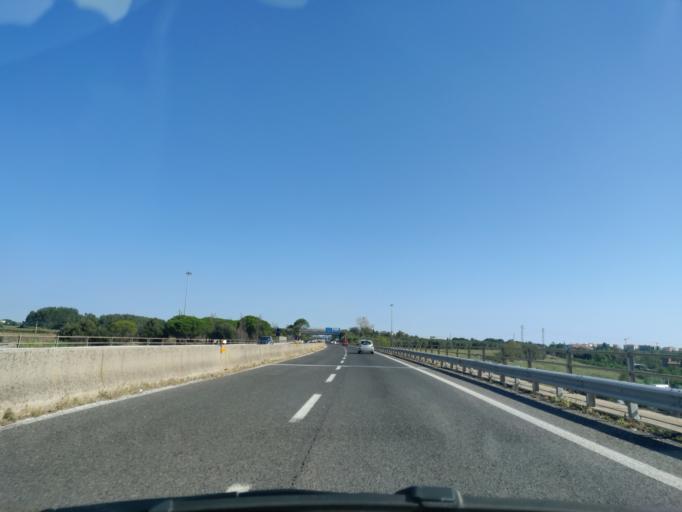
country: IT
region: Latium
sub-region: Provincia di Viterbo
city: Viterbo
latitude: 42.4159
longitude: 12.0769
